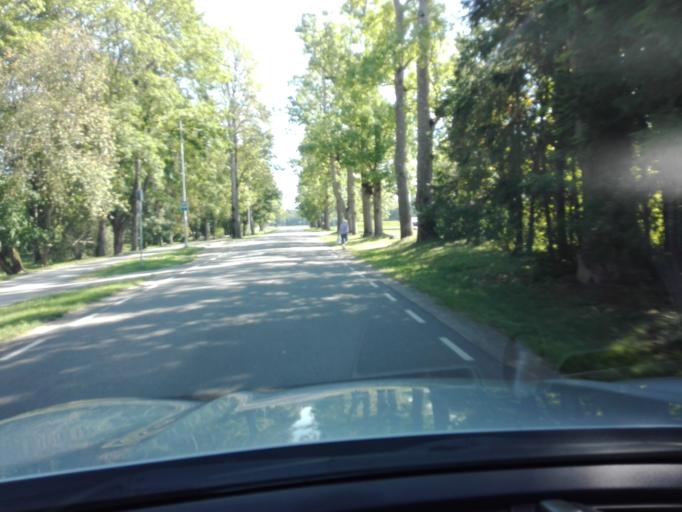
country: EE
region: Raplamaa
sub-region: Rapla vald
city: Rapla
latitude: 59.0215
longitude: 24.7643
